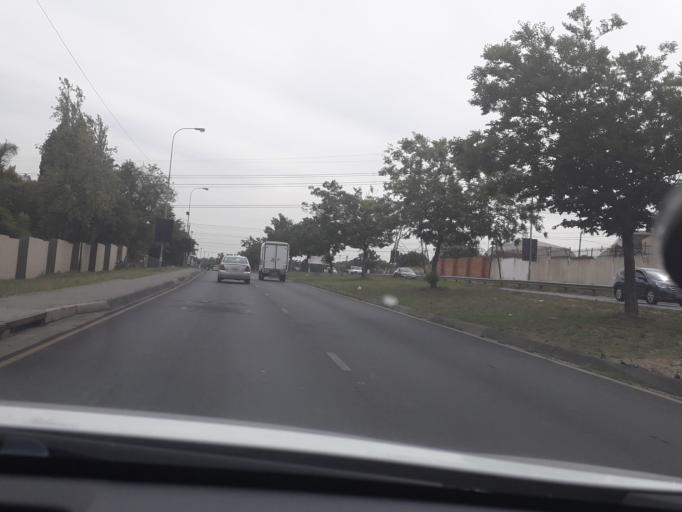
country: ZA
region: Gauteng
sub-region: City of Johannesburg Metropolitan Municipality
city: Johannesburg
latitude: -26.0939
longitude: 28.0192
